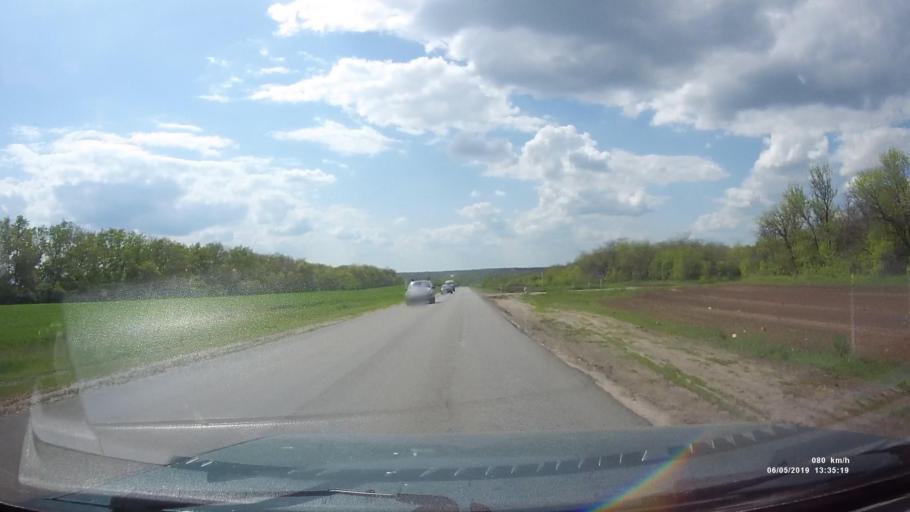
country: RU
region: Rostov
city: Ust'-Donetskiy
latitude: 47.6930
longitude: 40.7463
